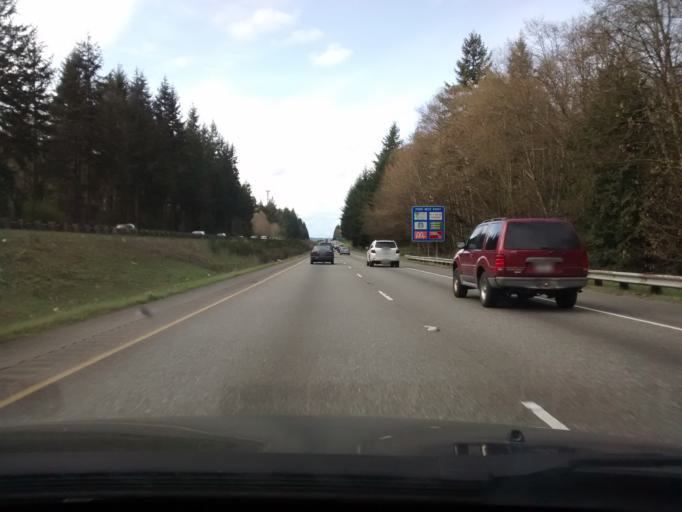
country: US
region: Washington
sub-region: Pierce County
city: Gig Harbor
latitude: 47.3415
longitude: -122.6067
